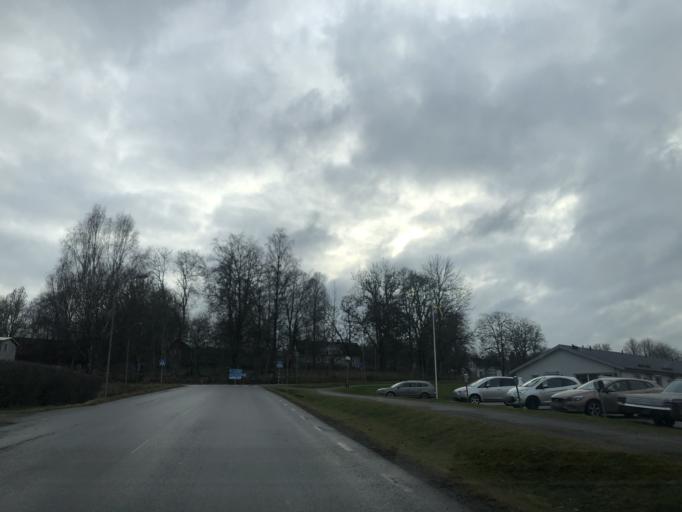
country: SE
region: Vaestra Goetaland
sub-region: Ulricehamns Kommun
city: Ulricehamn
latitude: 57.8387
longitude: 13.2851
